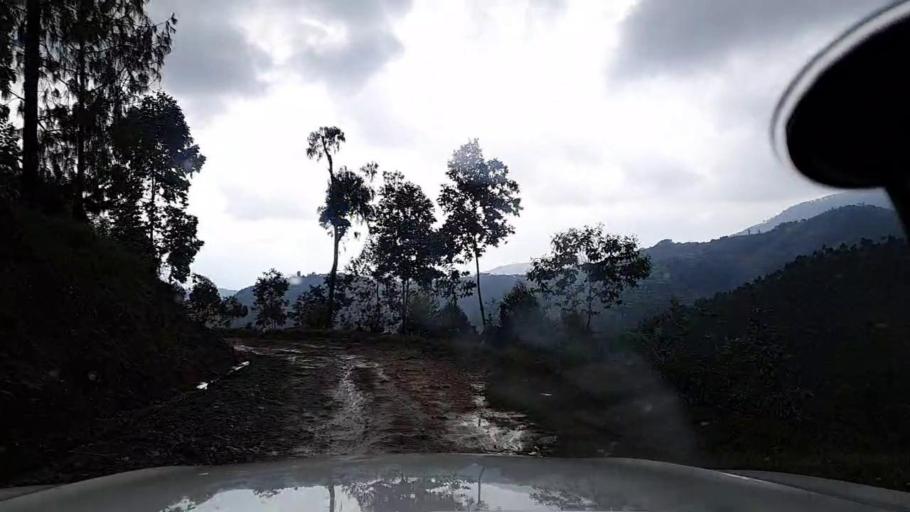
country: RW
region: Western Province
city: Kibuye
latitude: -2.0799
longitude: 29.5137
